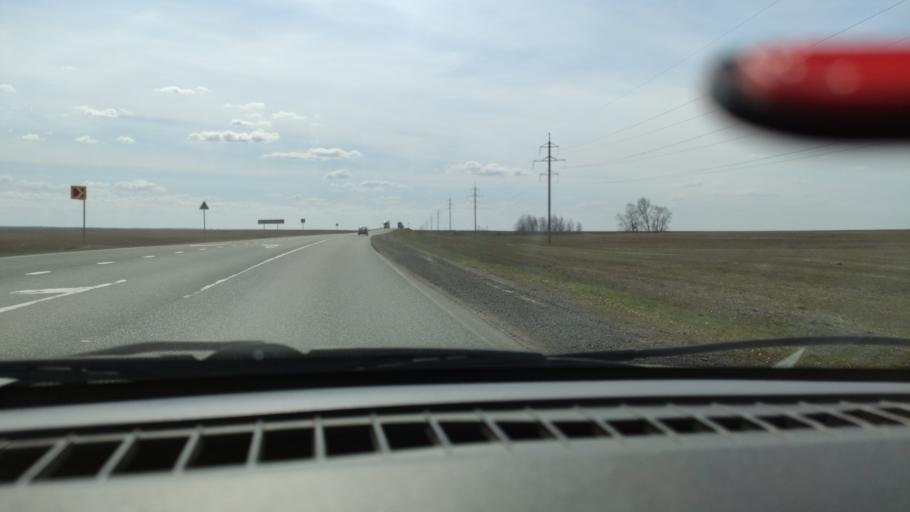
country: RU
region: Bashkortostan
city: Kushnarenkovo
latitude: 55.1744
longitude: 55.1272
